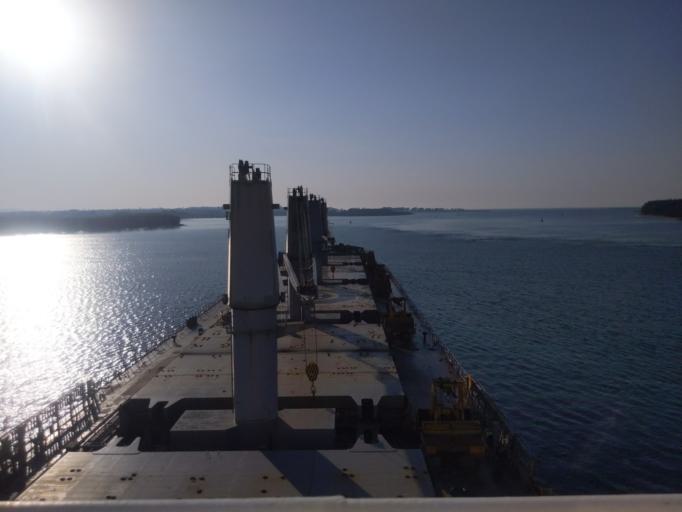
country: ZA
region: KwaZulu-Natal
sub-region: uThungulu District Municipality
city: Richards Bay
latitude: -28.8009
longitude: 32.0589
